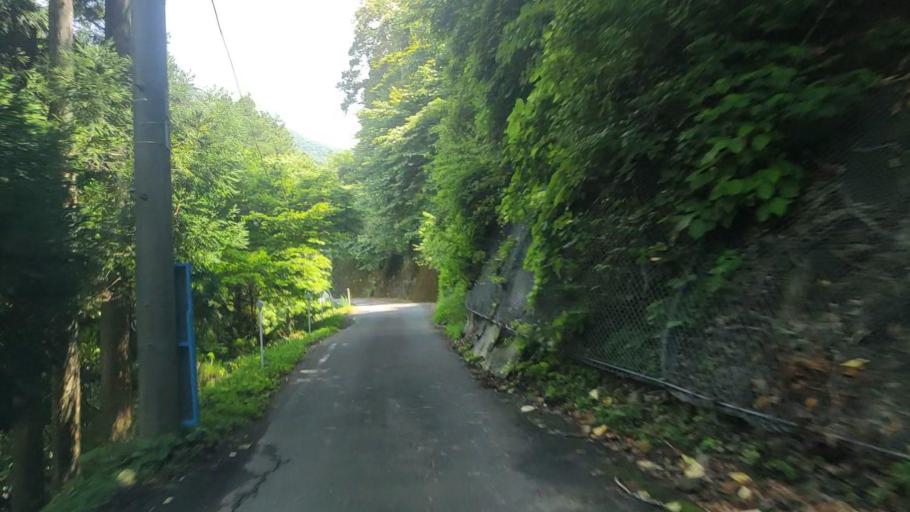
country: JP
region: Fukui
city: Ono
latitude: 35.7200
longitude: 136.5830
